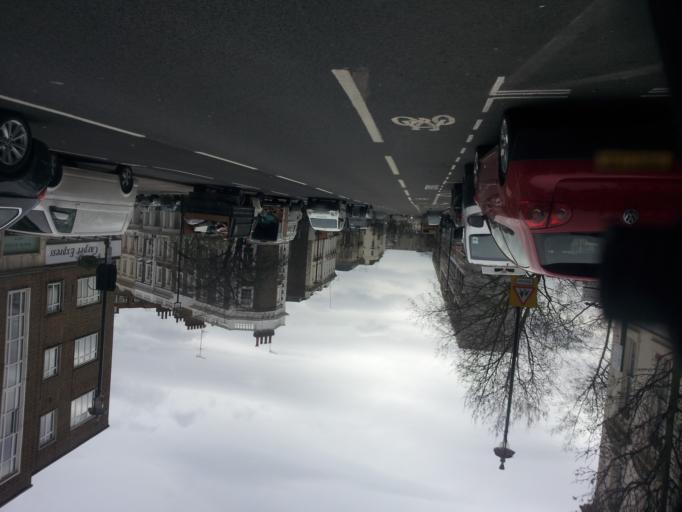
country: GB
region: England
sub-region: Greater London
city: Battersea
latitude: 51.4881
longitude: -0.1389
